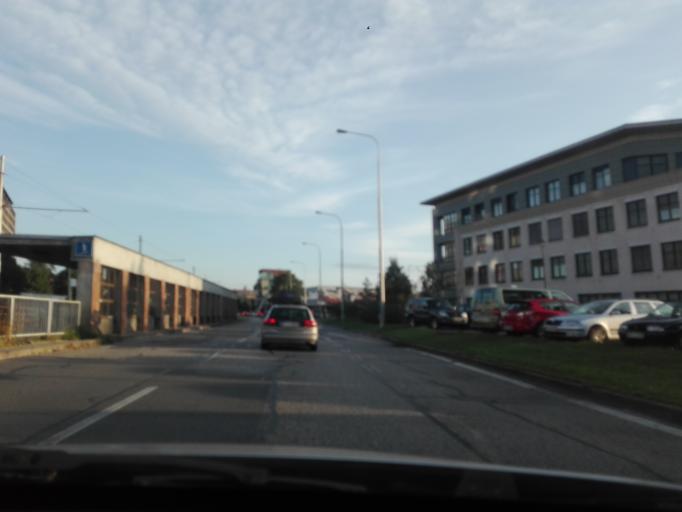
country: CZ
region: Moravskoslezsky
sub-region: Okres Ostrava-Mesto
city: Ostrava
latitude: 49.7861
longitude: 18.2564
